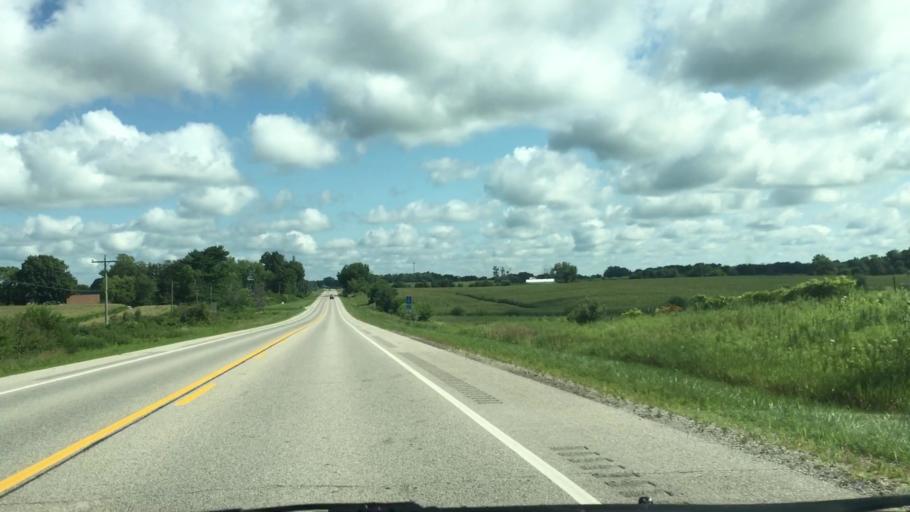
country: US
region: Iowa
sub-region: Johnson County
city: Iowa City
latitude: 41.7231
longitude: -91.4783
